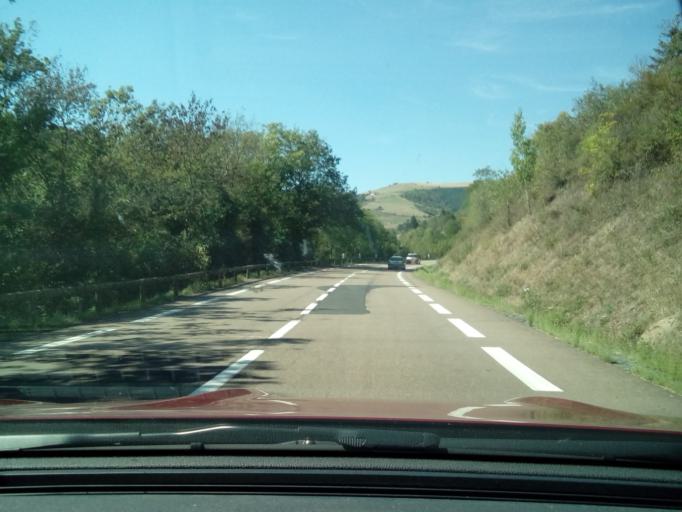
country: FR
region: Rhone-Alpes
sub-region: Departement du Rhone
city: Saint-Verand
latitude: 45.9158
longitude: 4.4922
